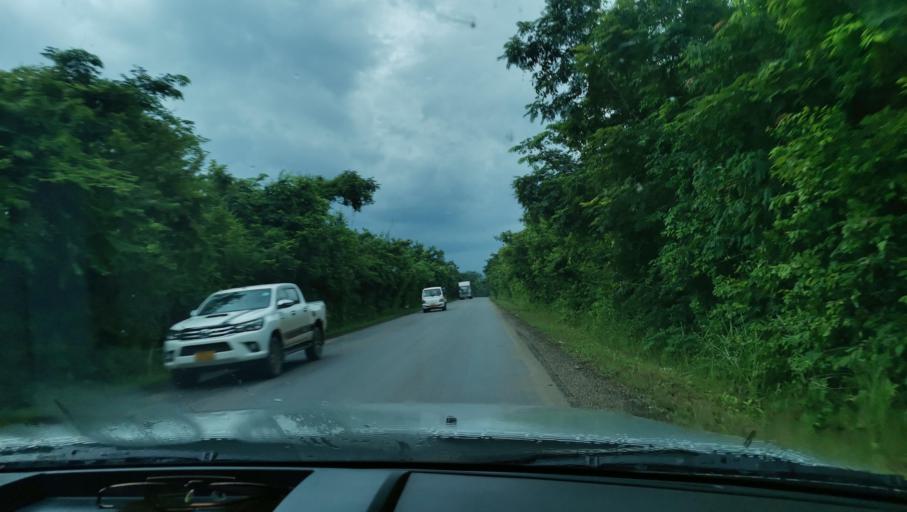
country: TH
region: Nakhon Phanom
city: Ban Phaeng
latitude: 17.8745
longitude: 104.4141
